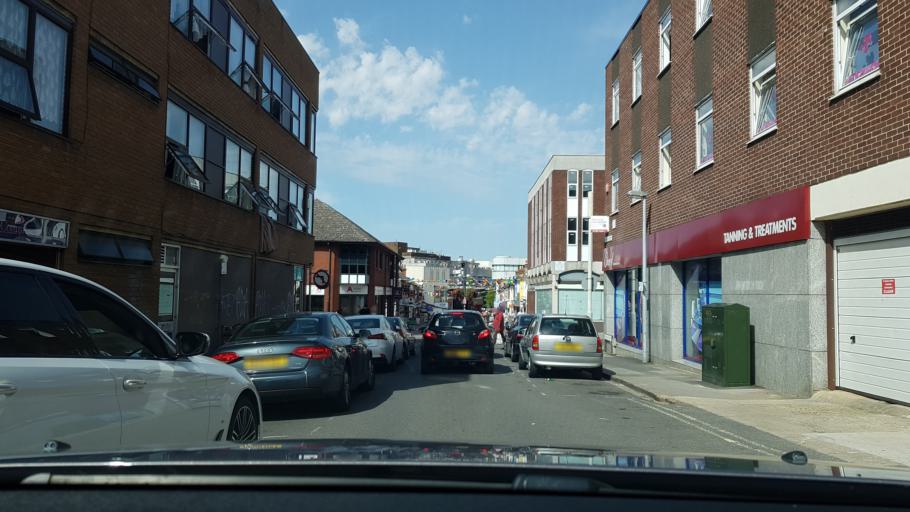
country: GB
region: England
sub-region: Borough of Swindon
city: Swindon
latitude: 51.5586
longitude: -1.7858
